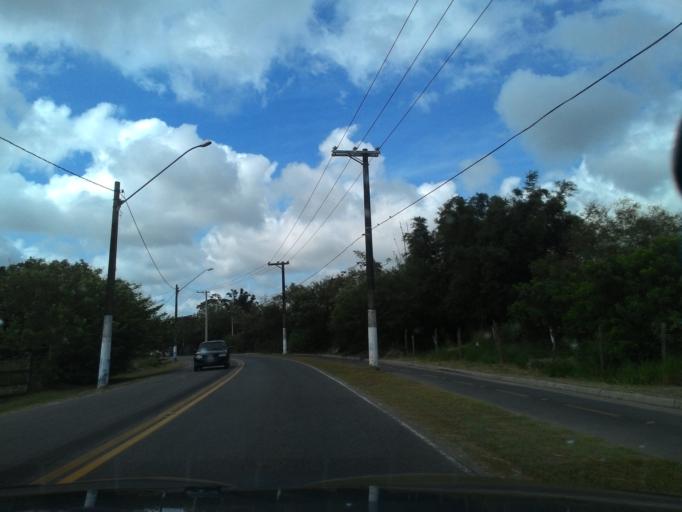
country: BR
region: Sao Paulo
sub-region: Iguape
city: Iguape
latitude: -24.6963
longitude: -47.5710
